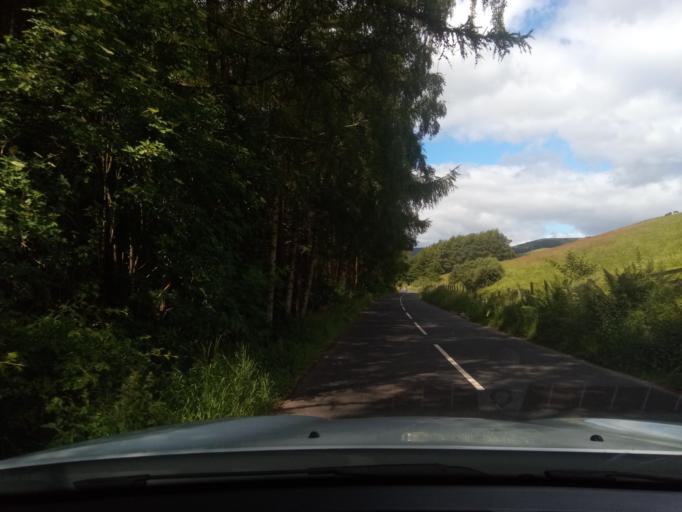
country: GB
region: Scotland
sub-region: The Scottish Borders
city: Selkirk
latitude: 55.5565
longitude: -2.9175
